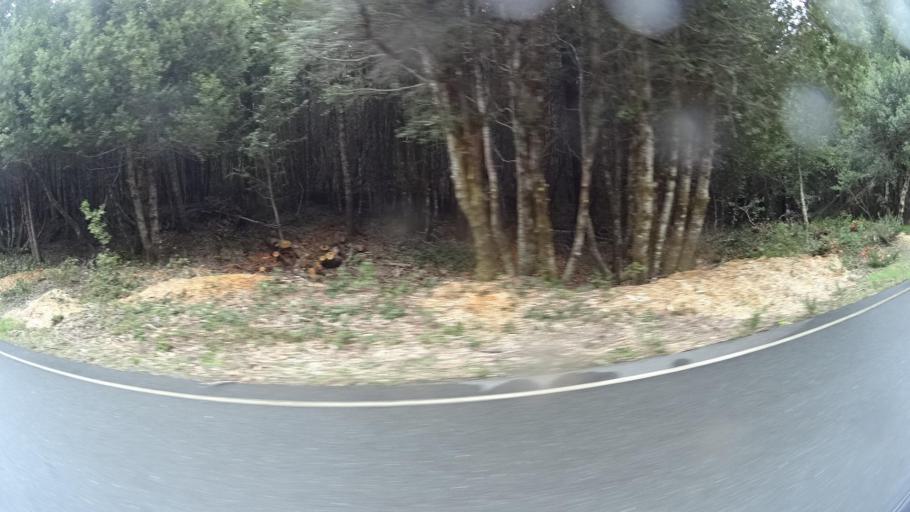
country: US
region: California
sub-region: Humboldt County
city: Willow Creek
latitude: 41.2000
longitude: -123.8049
